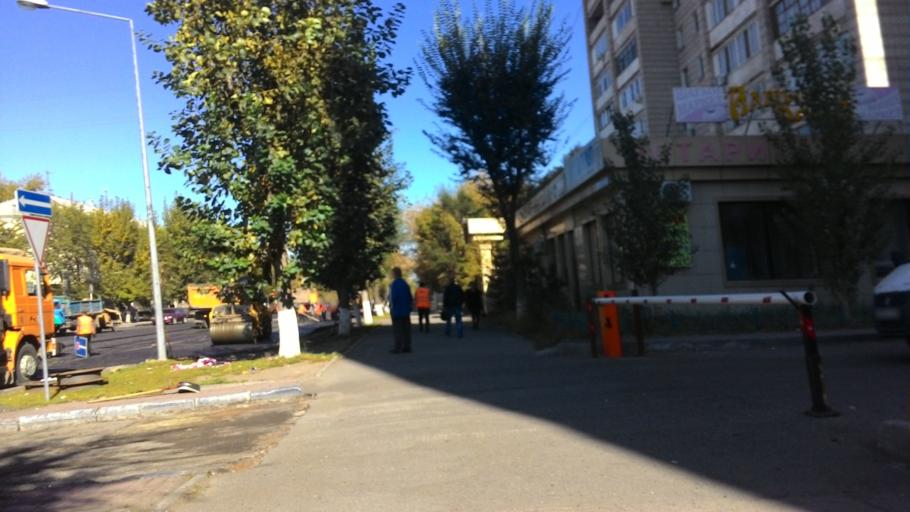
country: KZ
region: Astana Qalasy
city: Astana
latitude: 51.1679
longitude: 71.4162
